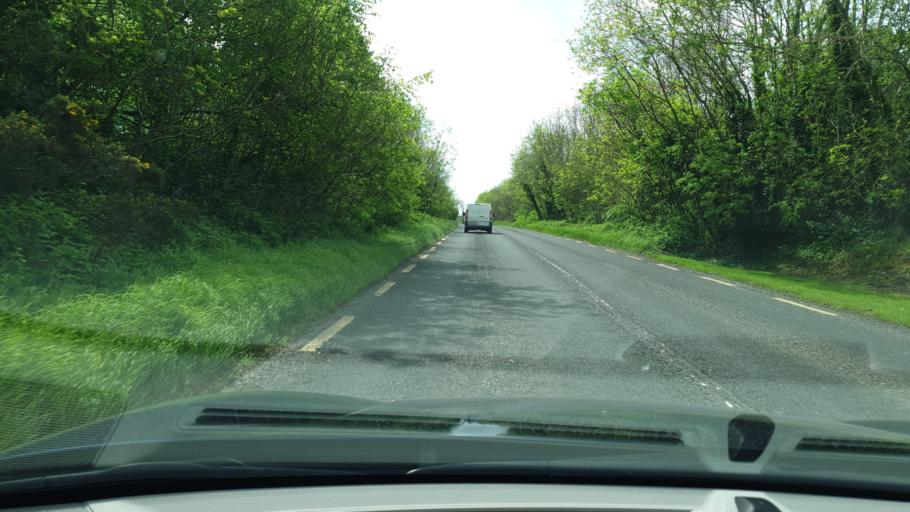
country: IE
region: Ulster
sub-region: An Cabhan
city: Kingscourt
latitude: 53.7980
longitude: -6.7382
